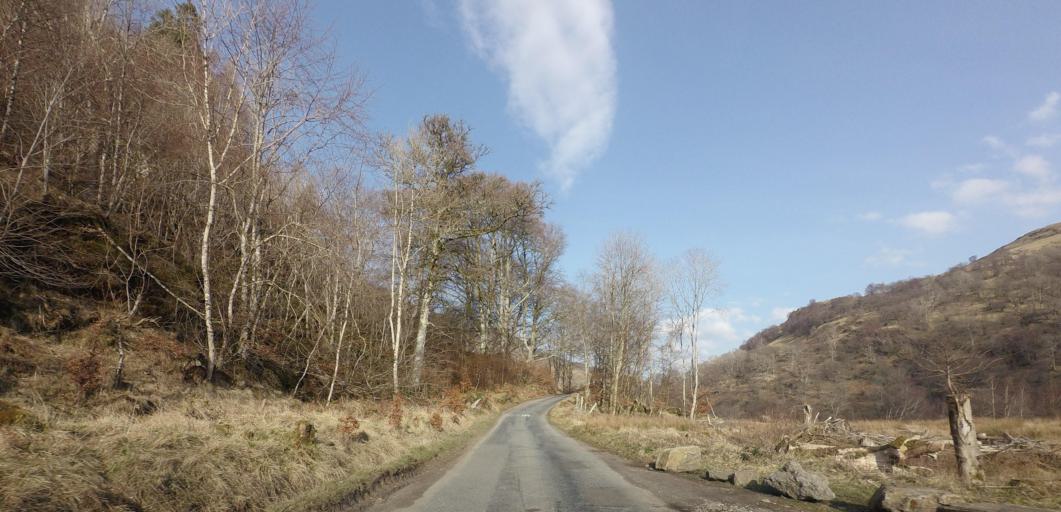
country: GB
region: Scotland
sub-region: Perth and Kinross
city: Aberfeldy
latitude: 56.5988
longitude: -4.1038
